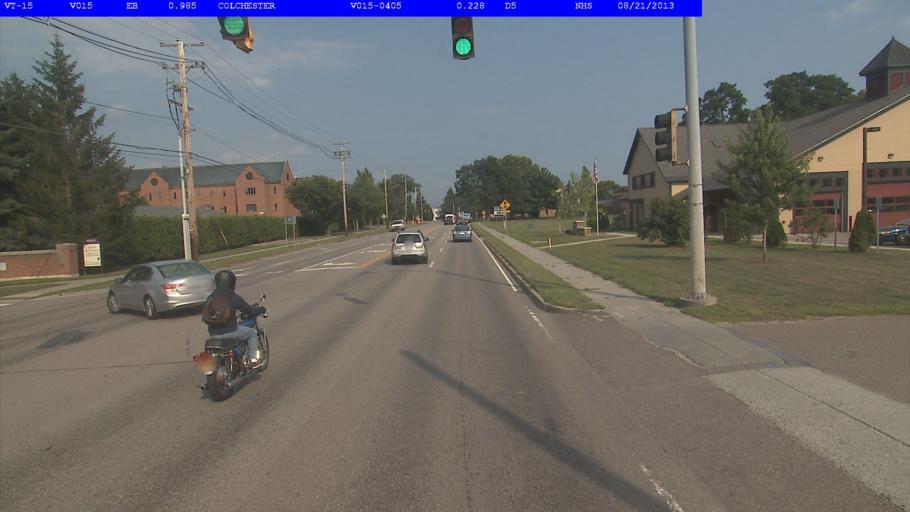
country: US
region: Vermont
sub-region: Chittenden County
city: Winooski
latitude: 44.4930
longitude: -73.1670
